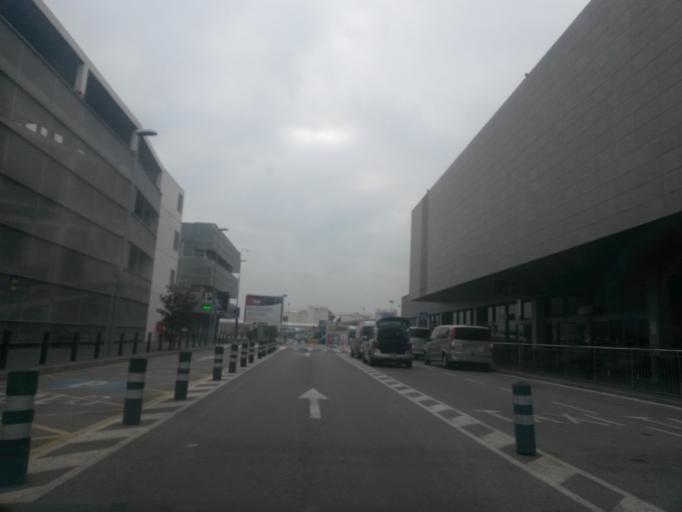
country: ES
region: Catalonia
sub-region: Provincia de Girona
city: Vilobi d'Onyar
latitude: 41.8976
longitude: 2.7663
